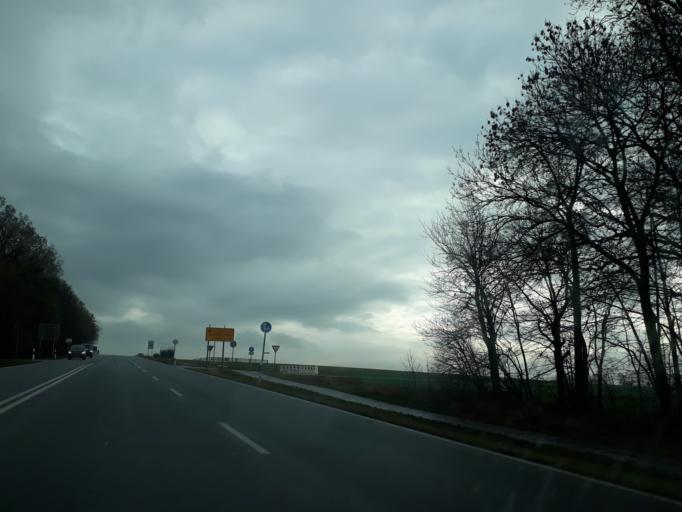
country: DE
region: Saxony
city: Hochkirch
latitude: 51.1292
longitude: 14.6172
